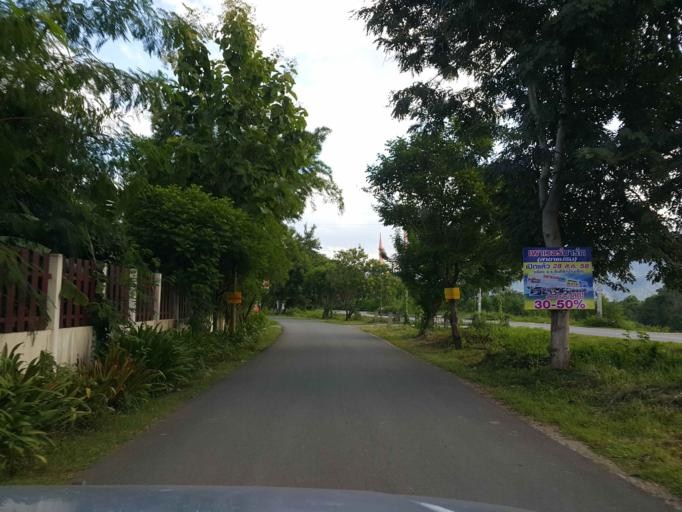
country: TH
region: Chiang Mai
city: San Sai
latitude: 18.9032
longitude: 98.9772
